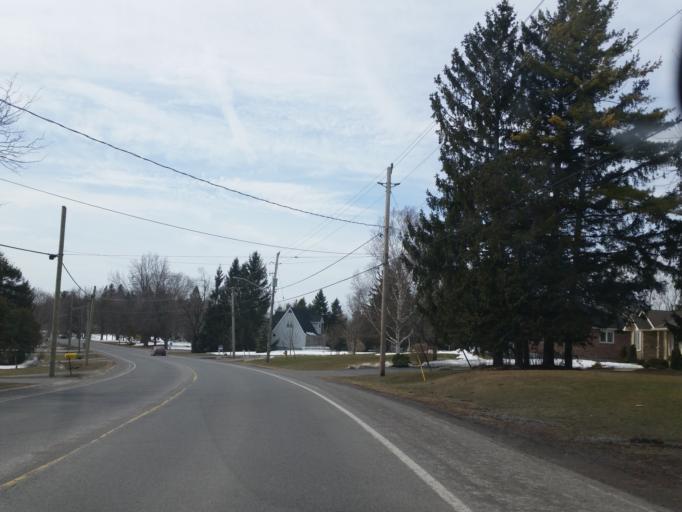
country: CA
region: Ontario
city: Napanee Downtown
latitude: 44.2375
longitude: -76.9684
